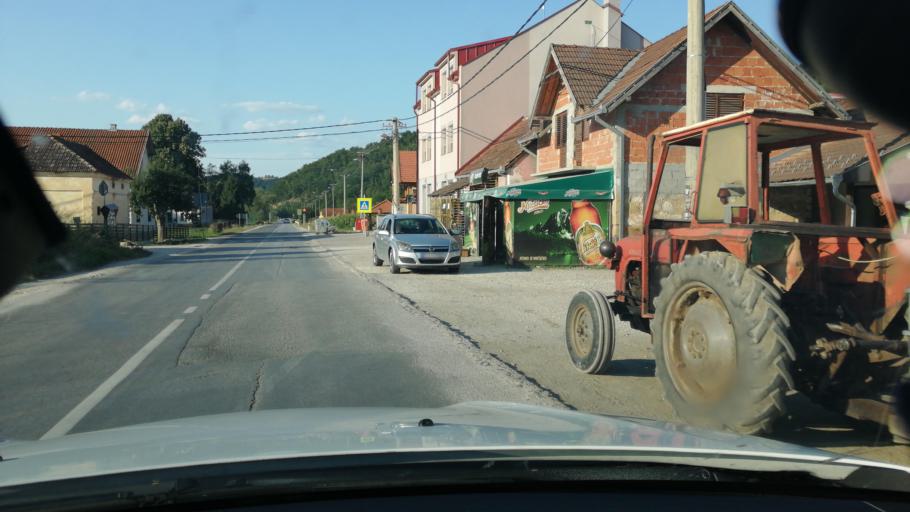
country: RS
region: Central Serbia
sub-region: Zlatiborski Okrug
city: Arilje
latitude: 43.7393
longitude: 20.2522
